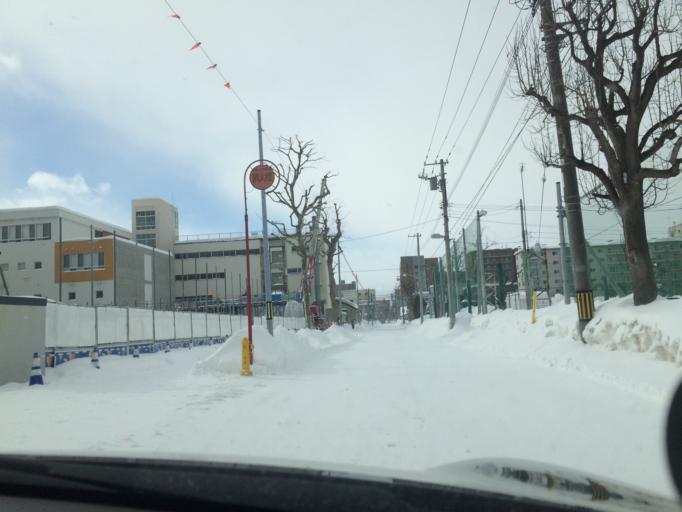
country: JP
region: Hokkaido
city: Sapporo
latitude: 43.0804
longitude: 141.3556
